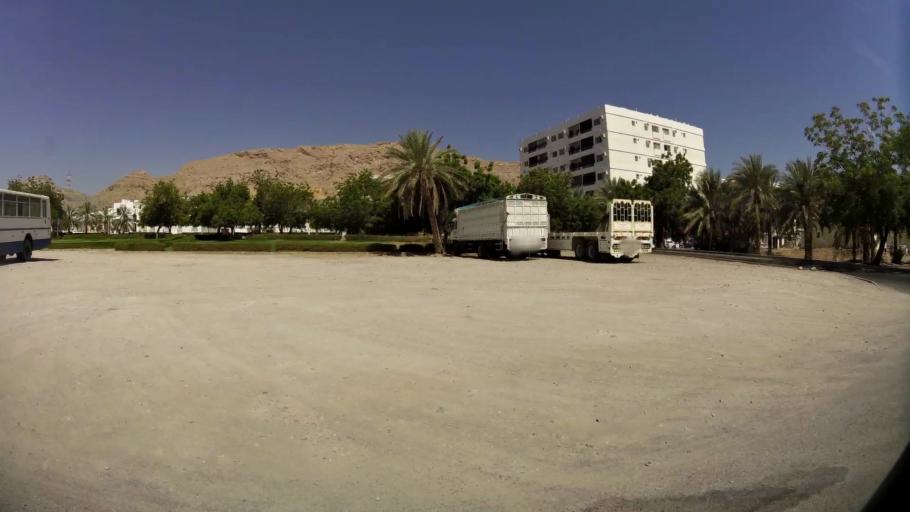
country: OM
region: Muhafazat Masqat
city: Muscat
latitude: 23.6013
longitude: 58.5382
